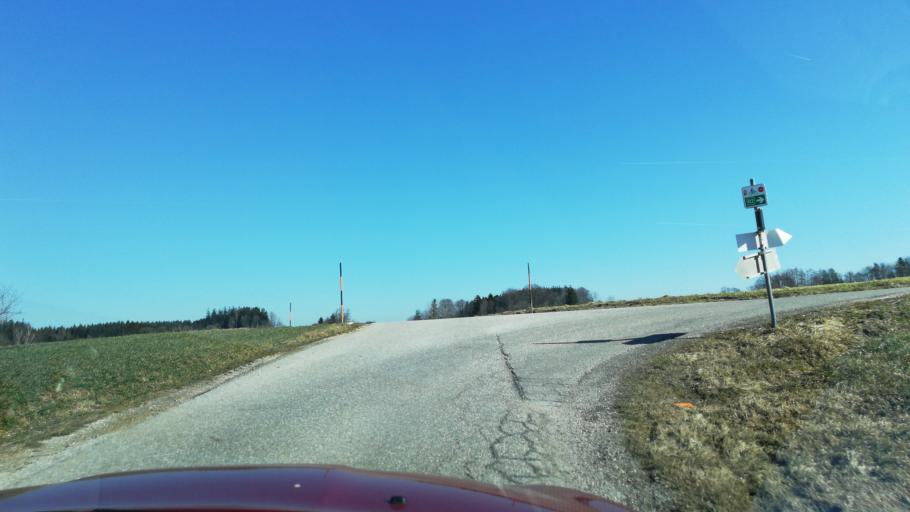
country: AT
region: Upper Austria
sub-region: Politischer Bezirk Vocklabruck
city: Aurach am Hongar
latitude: 47.9542
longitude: 13.6984
